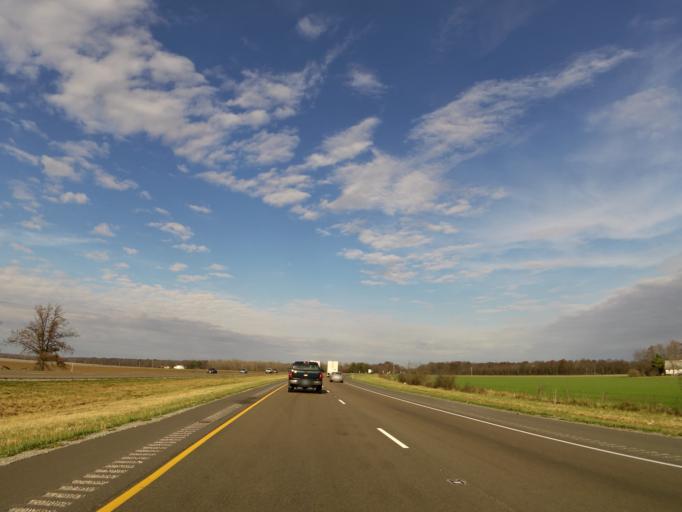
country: US
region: Illinois
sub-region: Washington County
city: Okawville
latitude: 38.4590
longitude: -89.5651
